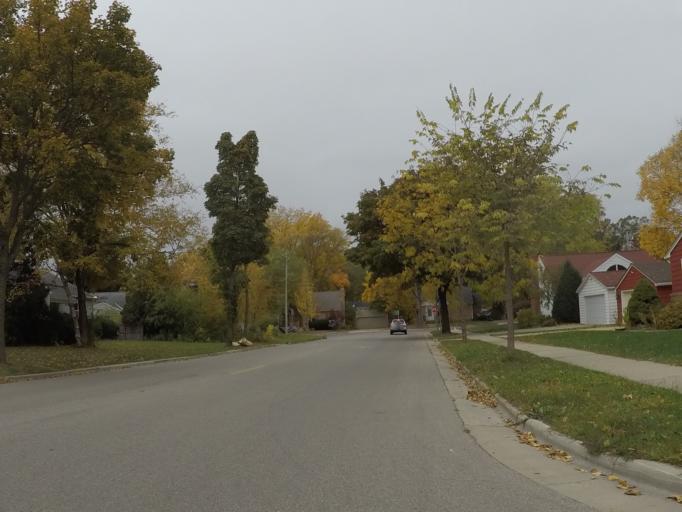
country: US
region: Wisconsin
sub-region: Dane County
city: Shorewood Hills
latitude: 43.0695
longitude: -89.4453
